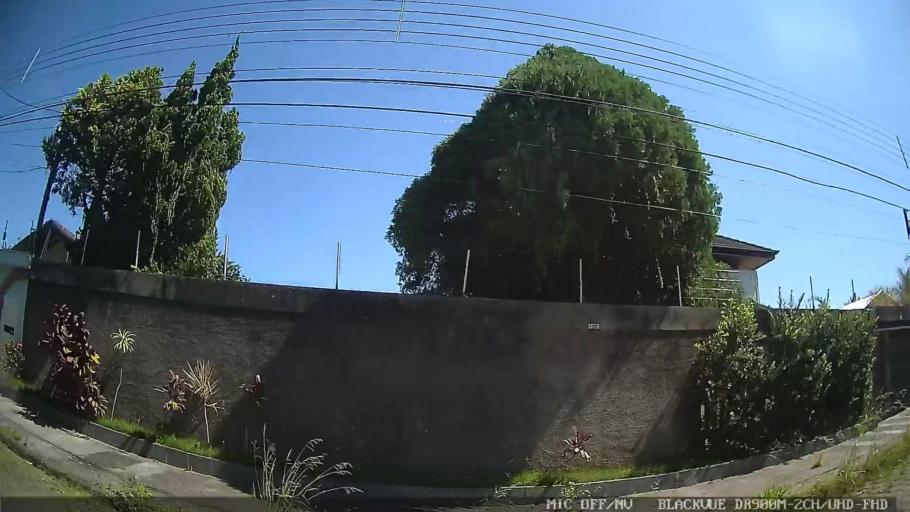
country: BR
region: Sao Paulo
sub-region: Peruibe
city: Peruibe
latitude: -24.2943
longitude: -46.9682
